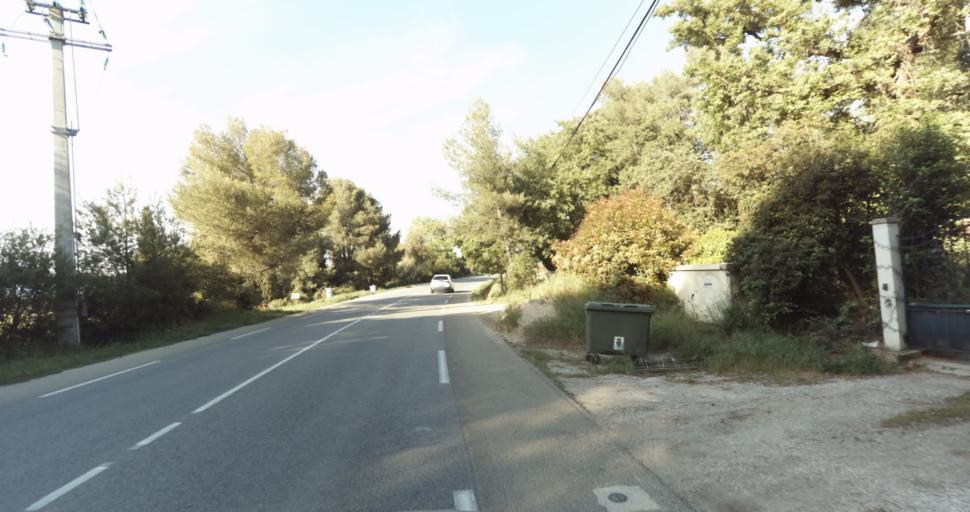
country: FR
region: Provence-Alpes-Cote d'Azur
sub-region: Departement du Var
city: Carqueiranne
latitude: 43.1150
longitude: 6.0566
